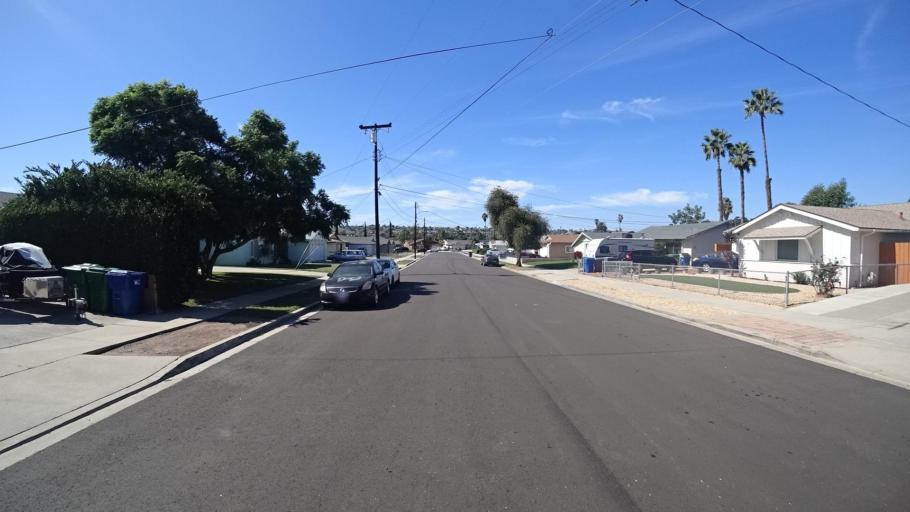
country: US
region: California
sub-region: San Diego County
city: La Presa
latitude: 32.7100
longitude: -117.0096
